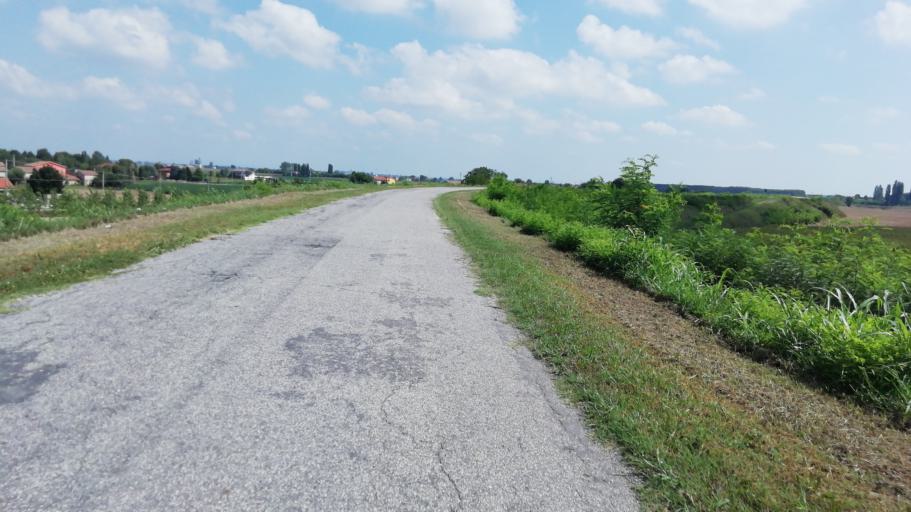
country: IT
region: Veneto
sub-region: Provincia di Rovigo
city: Gaiba
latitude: 44.9443
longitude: 11.4986
